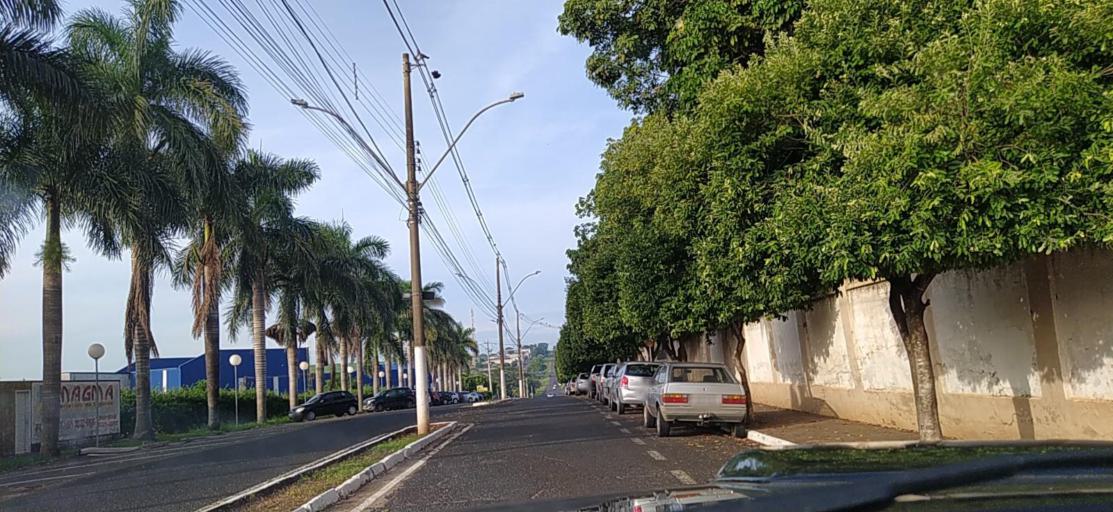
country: BR
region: Sao Paulo
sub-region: Pindorama
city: Pindorama
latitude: -21.1904
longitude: -48.9113
